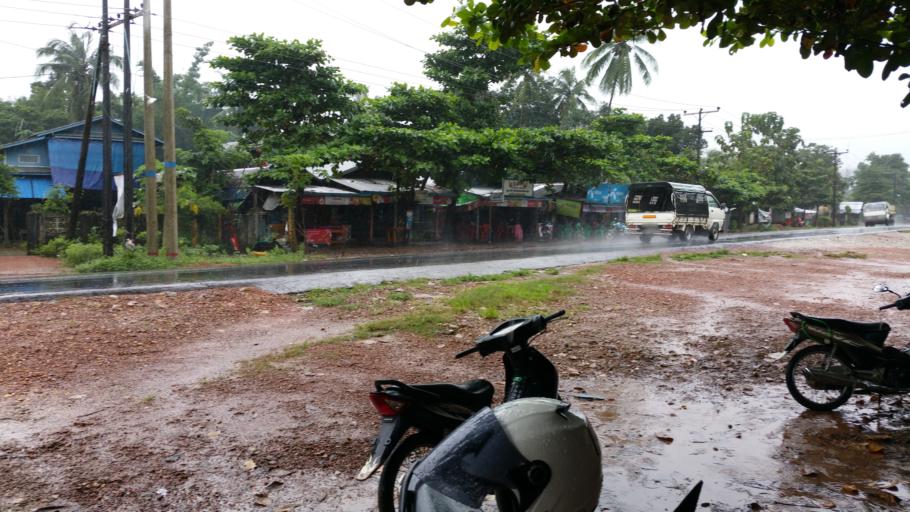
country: MM
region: Mon
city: Mudon
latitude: 16.3256
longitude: 97.6984
